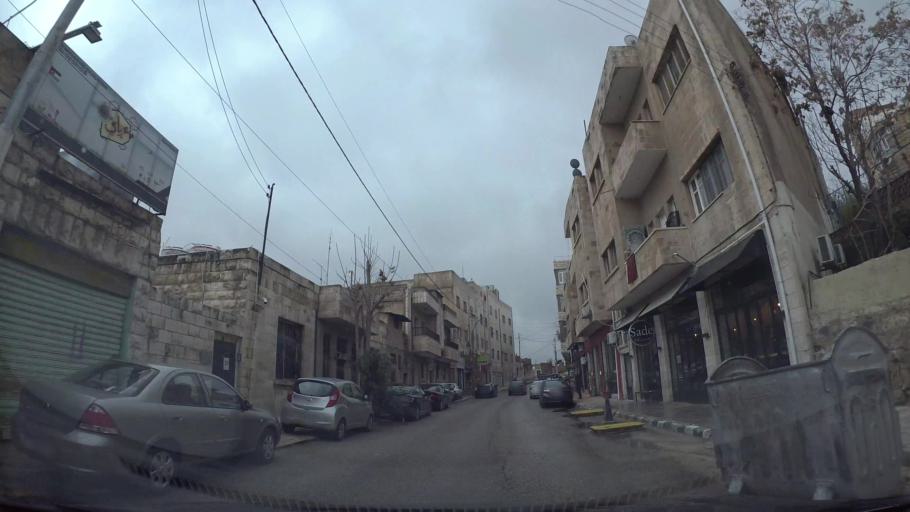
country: JO
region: Amman
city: Amman
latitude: 31.9469
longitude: 35.9305
